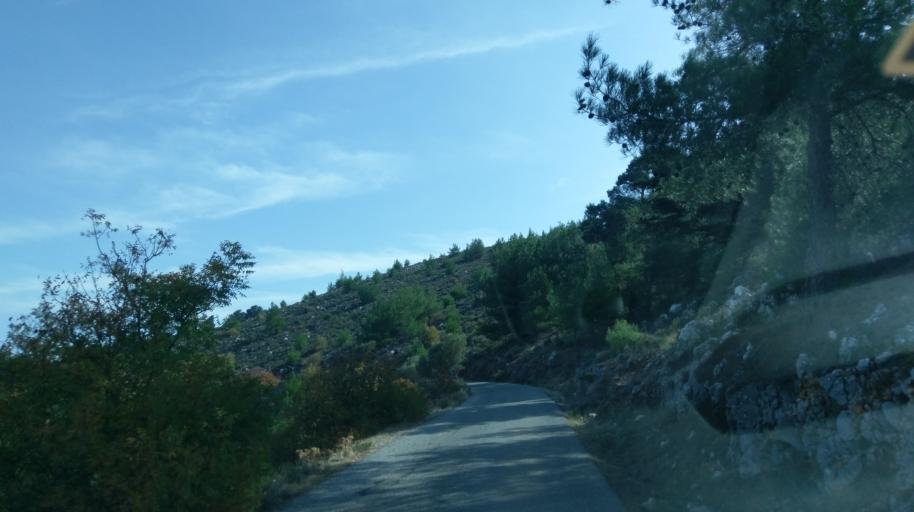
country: CY
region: Keryneia
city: Lapithos
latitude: 35.3076
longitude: 33.2152
